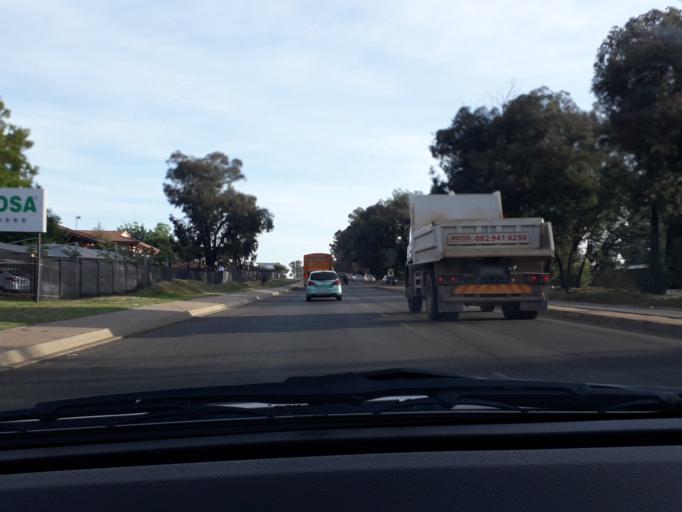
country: ZA
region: Gauteng
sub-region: City of Johannesburg Metropolitan Municipality
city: Midrand
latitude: -25.9479
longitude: 28.1424
